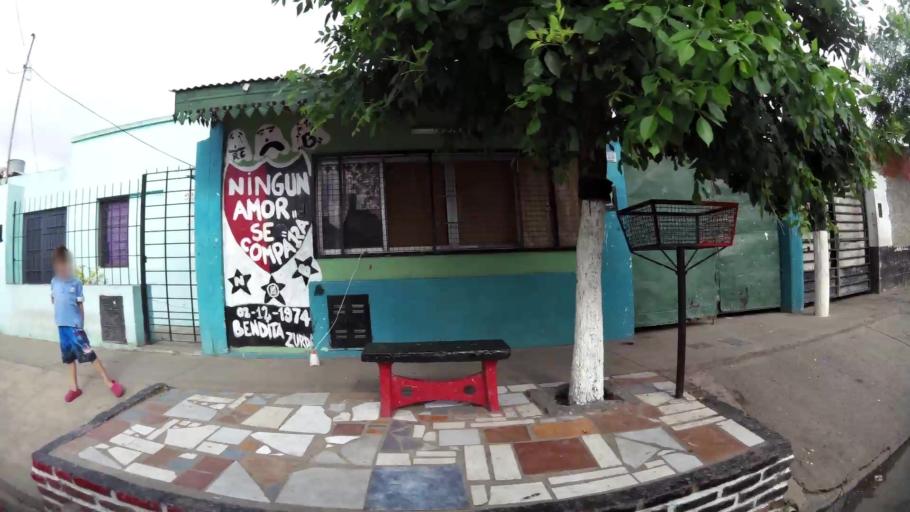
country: AR
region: Santa Fe
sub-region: Departamento de Rosario
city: Rosario
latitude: -32.9788
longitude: -60.6841
